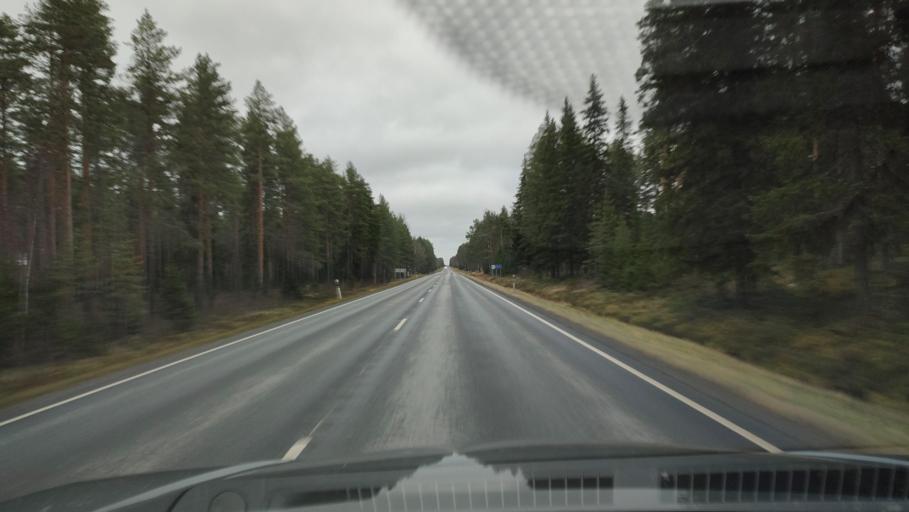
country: FI
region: Southern Ostrobothnia
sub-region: Seinaejoki
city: Kurikka
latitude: 62.5187
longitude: 22.3162
